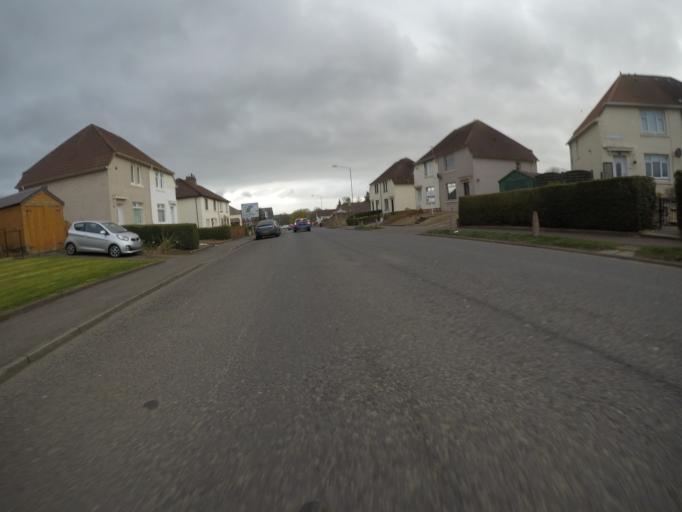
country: GB
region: Scotland
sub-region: East Ayrshire
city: Kilmarnock
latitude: 55.6117
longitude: -4.5158
